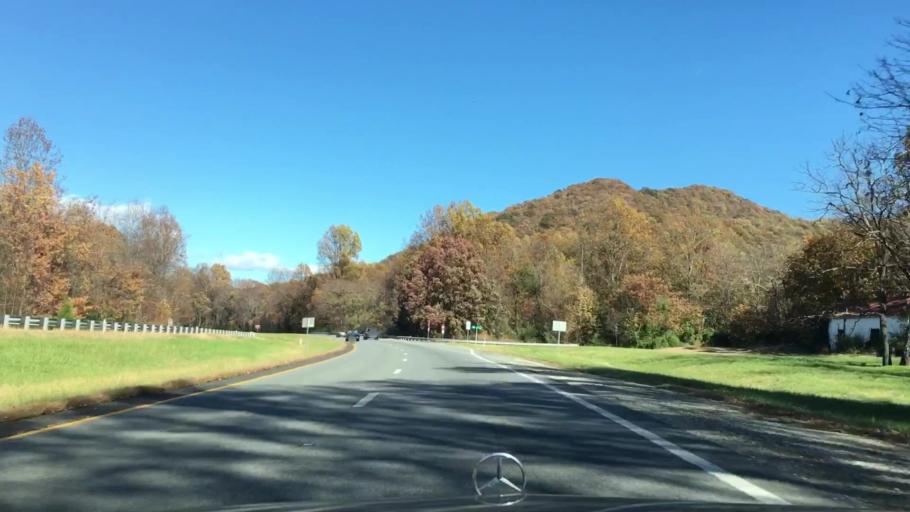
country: US
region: Virginia
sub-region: Nelson County
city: Nellysford
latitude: 37.8726
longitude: -78.7178
